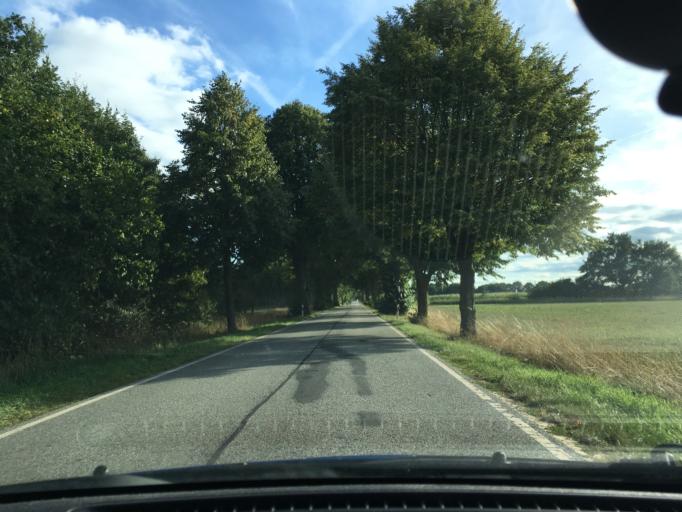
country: DE
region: Lower Saxony
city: Brackel
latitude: 53.3098
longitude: 10.0530
